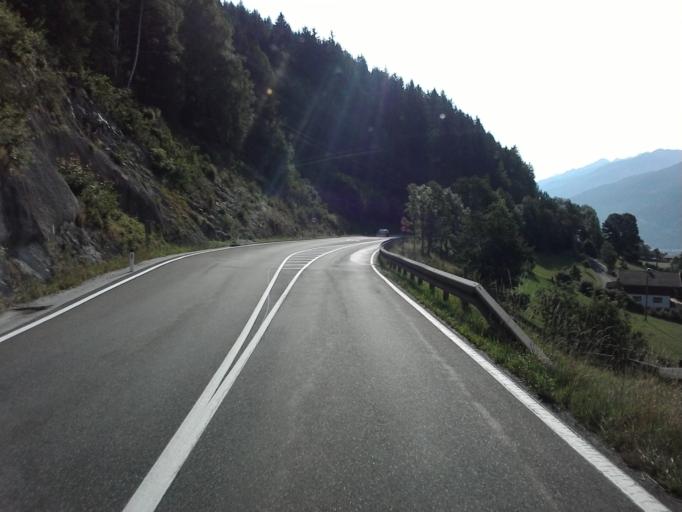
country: AT
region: Salzburg
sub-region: Politischer Bezirk Zell am See
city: Mittersill
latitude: 47.2888
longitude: 12.4487
